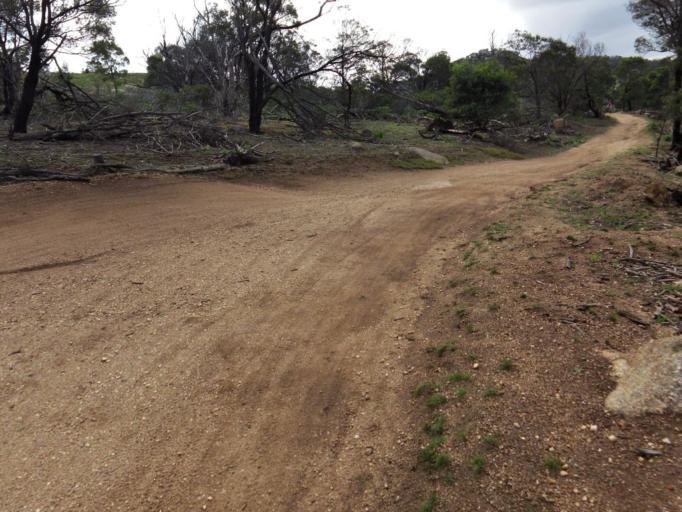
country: AU
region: Victoria
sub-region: Wyndham
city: Little River
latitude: -37.9311
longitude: 144.4300
